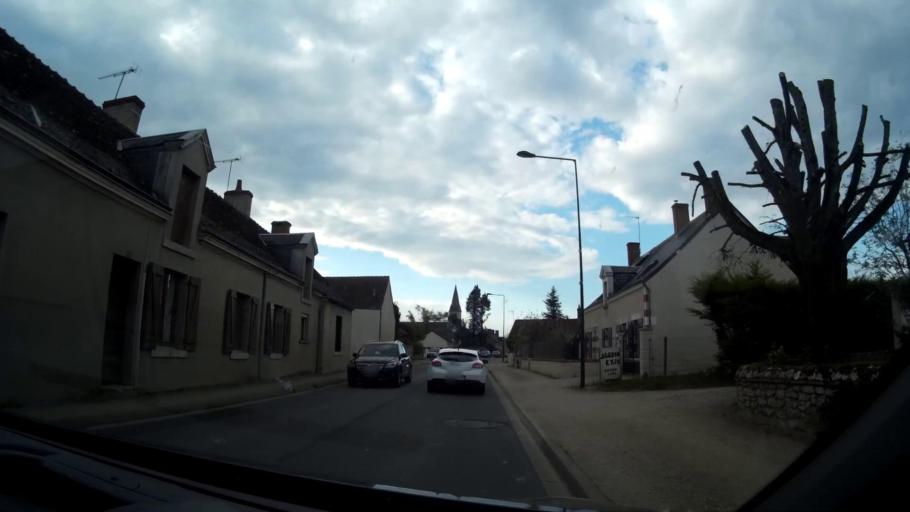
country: FR
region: Centre
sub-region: Departement du Loir-et-Cher
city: Cormeray
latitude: 47.4879
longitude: 1.4084
